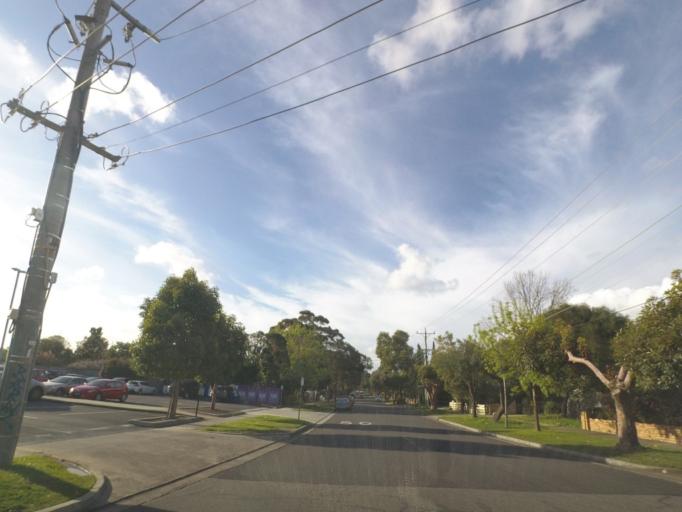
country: AU
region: Victoria
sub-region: Whitehorse
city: Blackburn South
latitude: -37.8315
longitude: 145.1485
